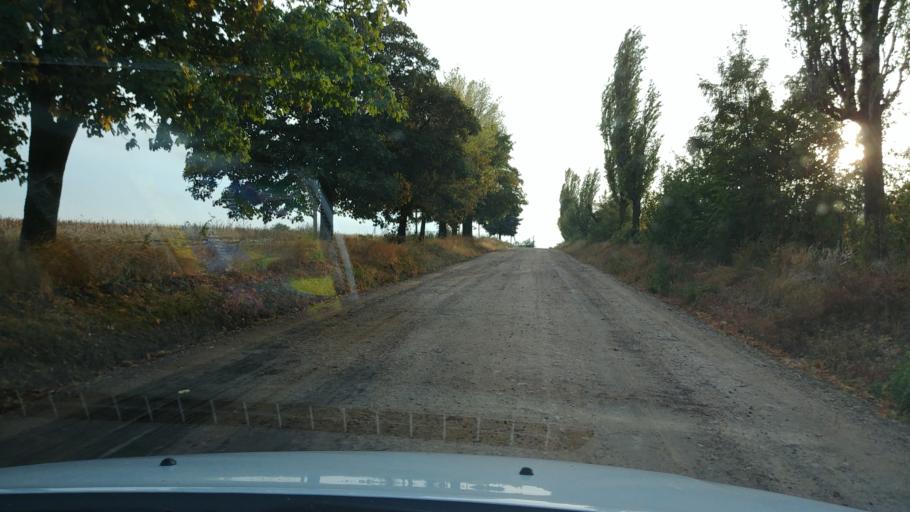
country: MD
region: Rezina
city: Saharna
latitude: 47.6791
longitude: 28.9674
